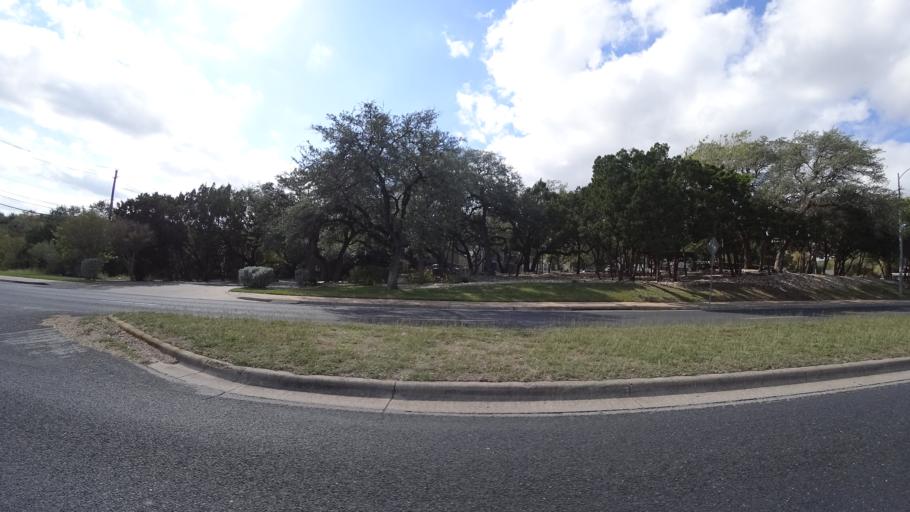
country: US
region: Texas
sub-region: Travis County
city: Wells Branch
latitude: 30.4112
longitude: -97.7208
